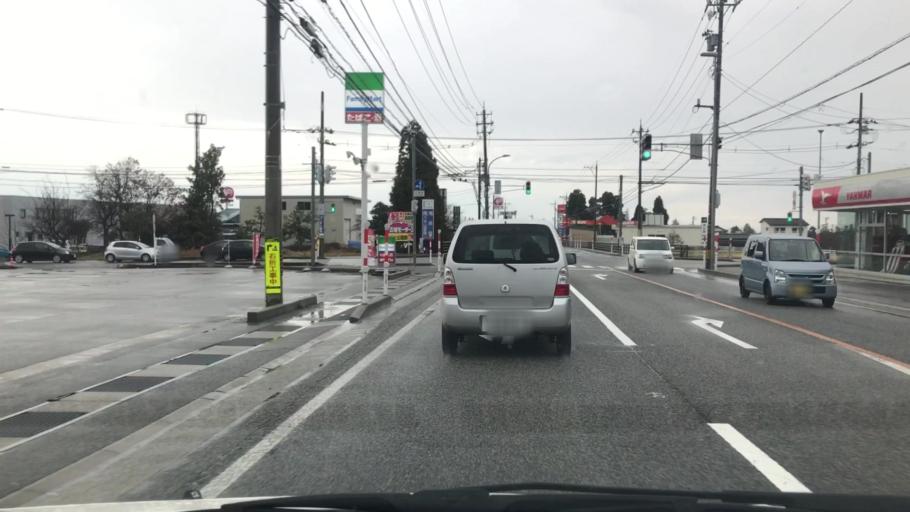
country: JP
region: Toyama
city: Yatsuomachi-higashikumisaka
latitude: 36.6044
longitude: 137.2034
